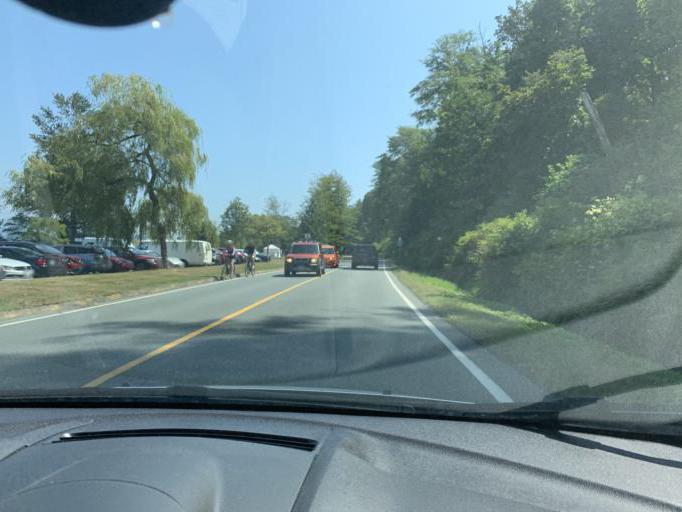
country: CA
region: British Columbia
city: West End
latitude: 49.2781
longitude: -123.2286
